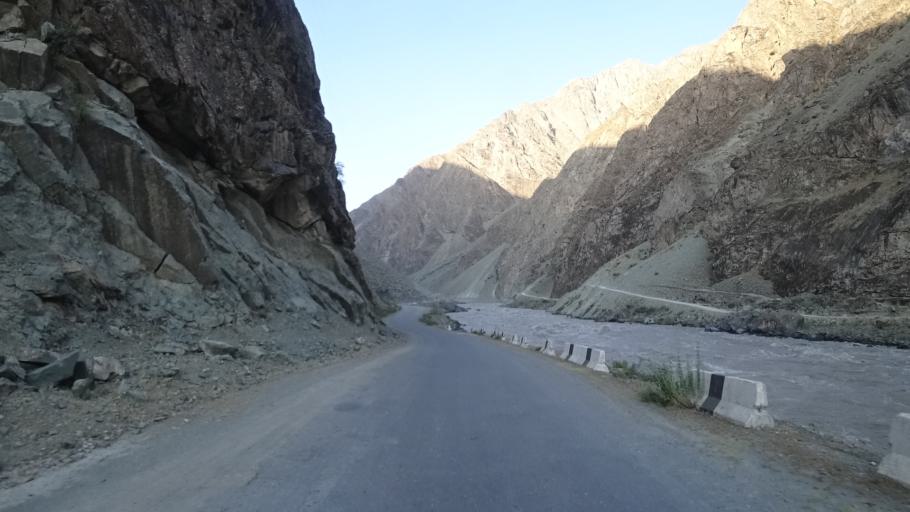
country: TJ
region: Gorno-Badakhshan
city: Qalaikhumb
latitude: 38.4230
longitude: 70.7450
